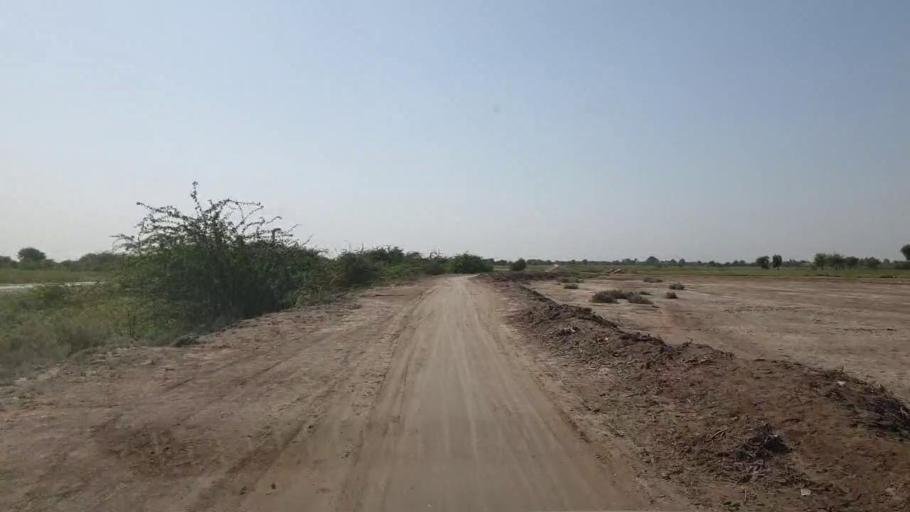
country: PK
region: Sindh
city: Tando Bago
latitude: 24.7392
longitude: 69.0222
